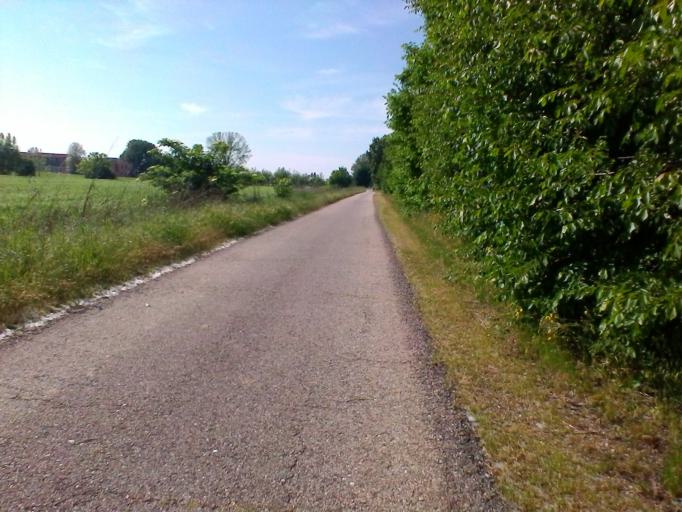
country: IT
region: Lombardy
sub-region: Provincia di Mantova
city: Marmirolo
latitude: 45.2347
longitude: 10.7282
